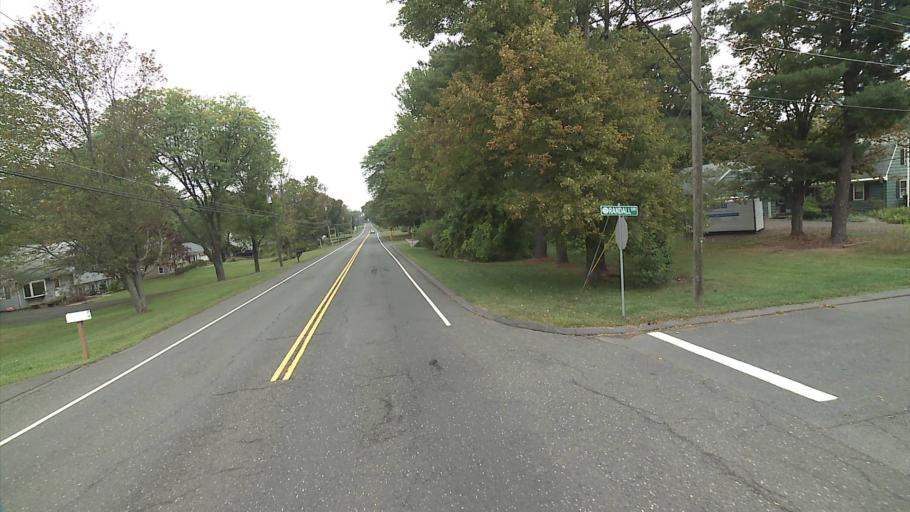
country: US
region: Connecticut
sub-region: Hartford County
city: Suffield Depot
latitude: 42.0166
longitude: -72.6405
